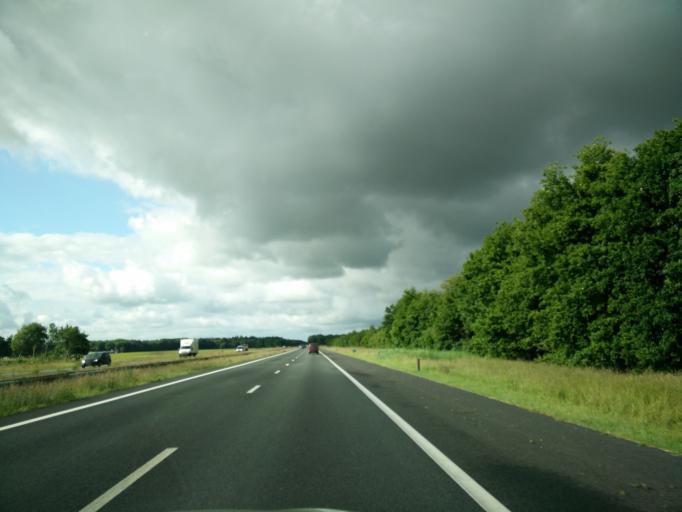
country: NL
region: Drenthe
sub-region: Gemeente Assen
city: Assen
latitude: 52.9381
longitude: 6.5376
